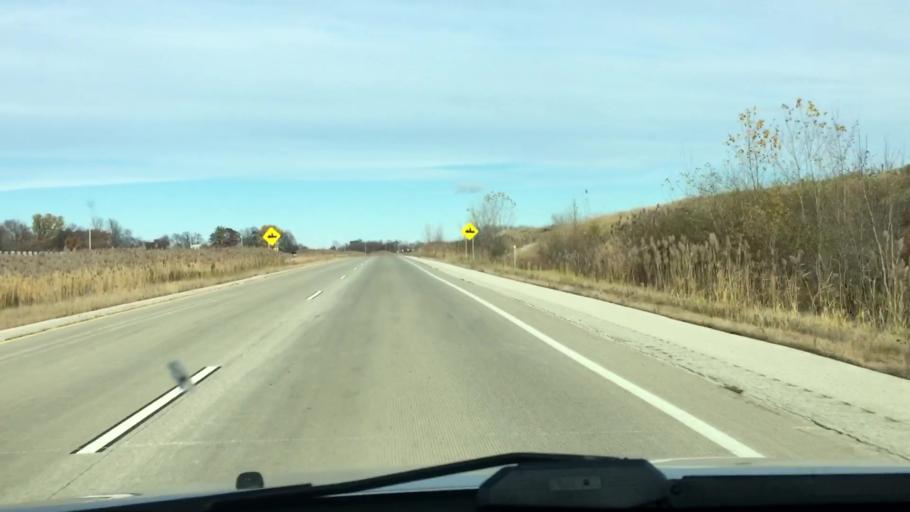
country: US
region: Wisconsin
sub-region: Kewaunee County
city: Luxemburg
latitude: 44.6691
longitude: -87.7407
